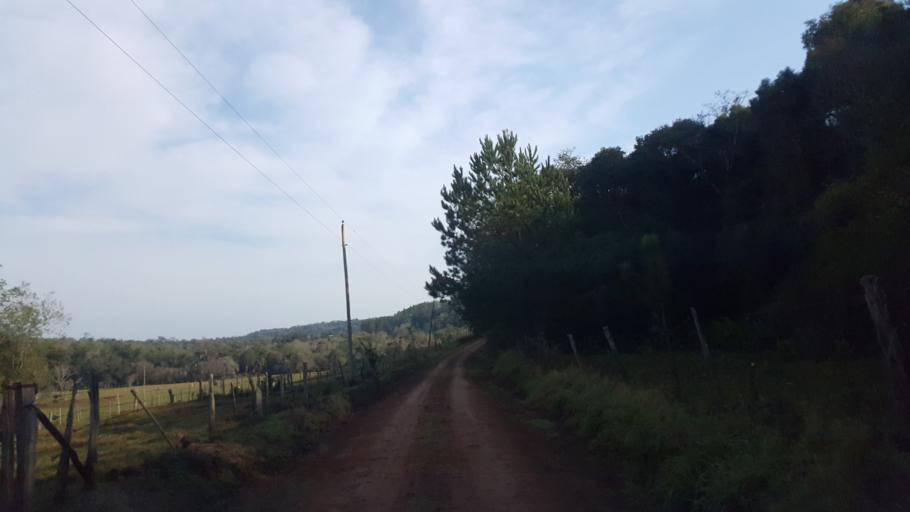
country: AR
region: Misiones
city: Capiovi
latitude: -26.9138
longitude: -55.0826
